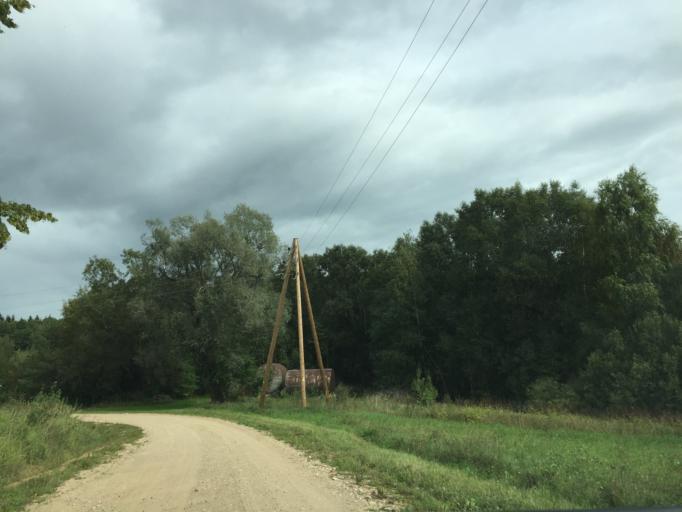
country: LV
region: Pargaujas
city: Stalbe
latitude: 57.5140
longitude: 24.9171
